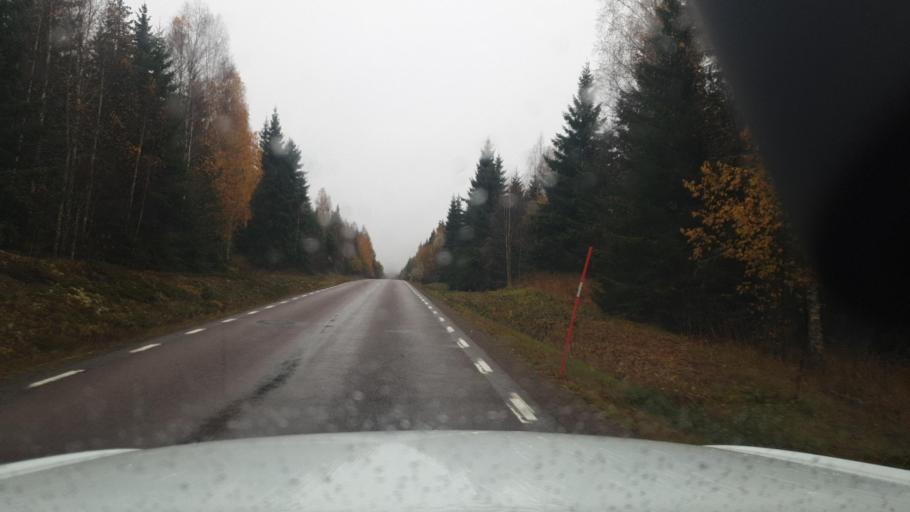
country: SE
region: Vaermland
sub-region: Torsby Kommun
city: Torsby
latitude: 59.9476
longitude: 12.7384
